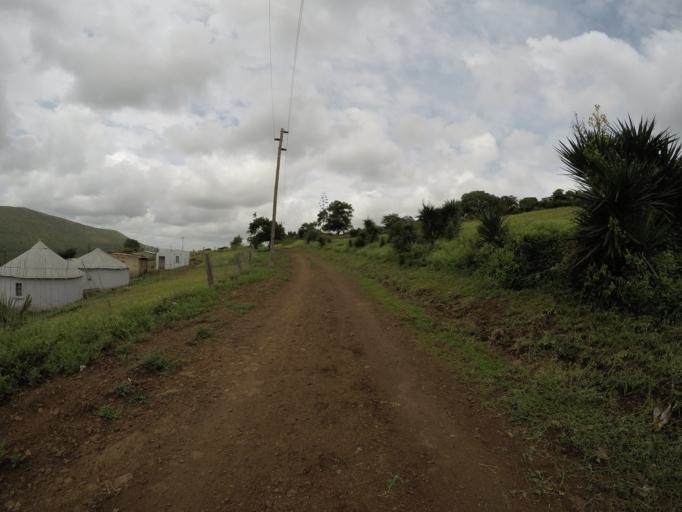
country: ZA
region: KwaZulu-Natal
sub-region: uThungulu District Municipality
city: Empangeni
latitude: -28.5869
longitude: 31.8888
